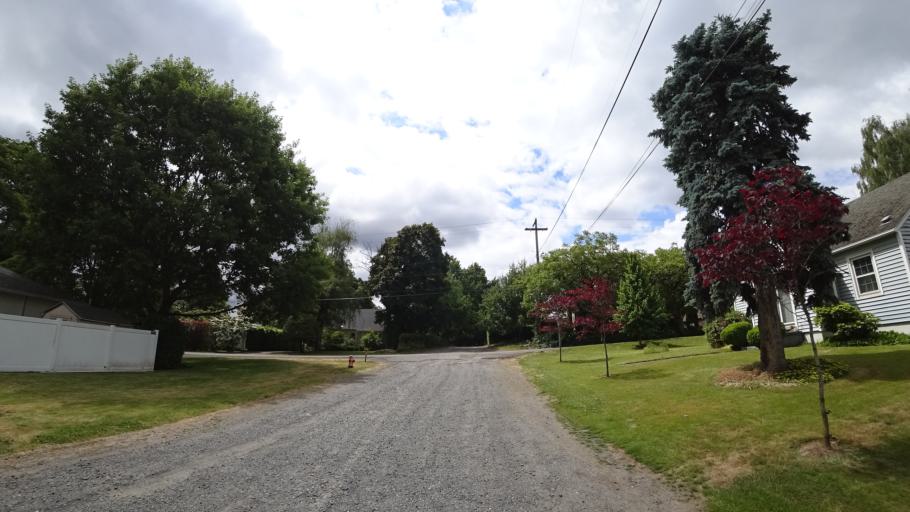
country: US
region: Oregon
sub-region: Multnomah County
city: Portland
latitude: 45.5654
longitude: -122.6044
